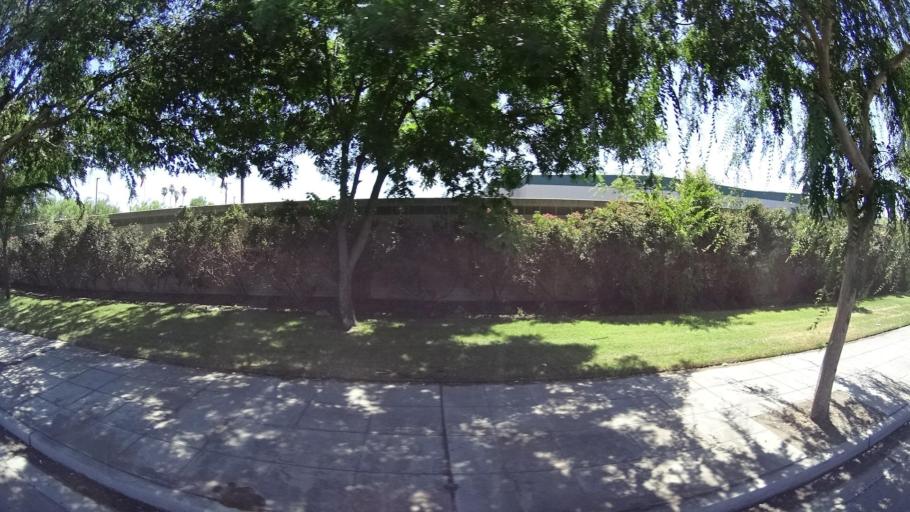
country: US
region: California
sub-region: Fresno County
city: Fresno
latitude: 36.7027
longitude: -119.7906
